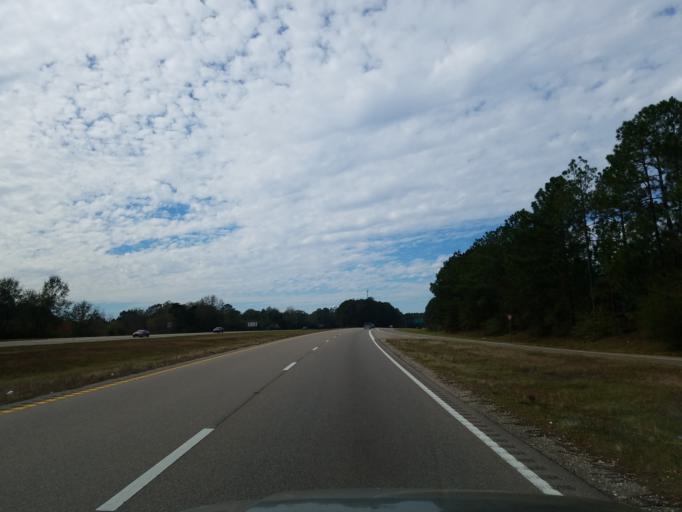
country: US
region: Mississippi
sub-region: Forrest County
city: Hattiesburg
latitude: 31.2391
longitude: -89.3049
